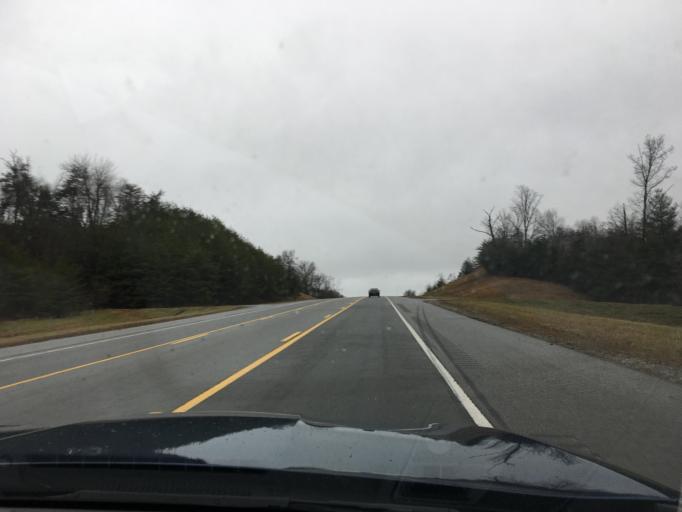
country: US
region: Tennessee
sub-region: Cumberland County
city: Crossville
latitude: 35.9380
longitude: -85.0007
